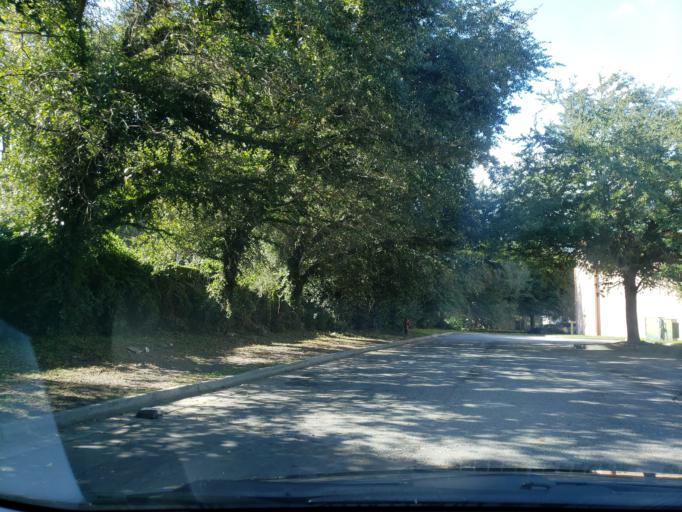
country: US
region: Georgia
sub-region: Chatham County
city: Montgomery
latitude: 31.9563
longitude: -81.0976
